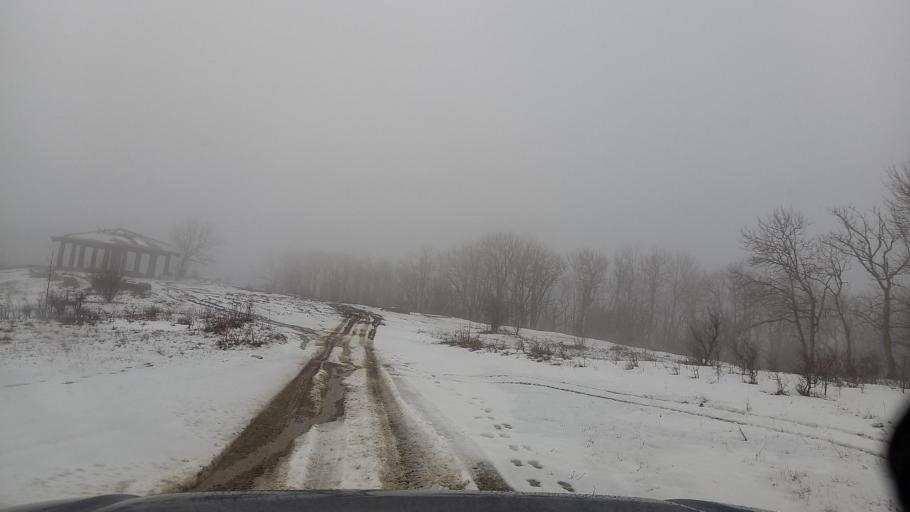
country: RU
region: Krasnodarskiy
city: Divnomorskoye
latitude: 44.6078
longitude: 38.2478
